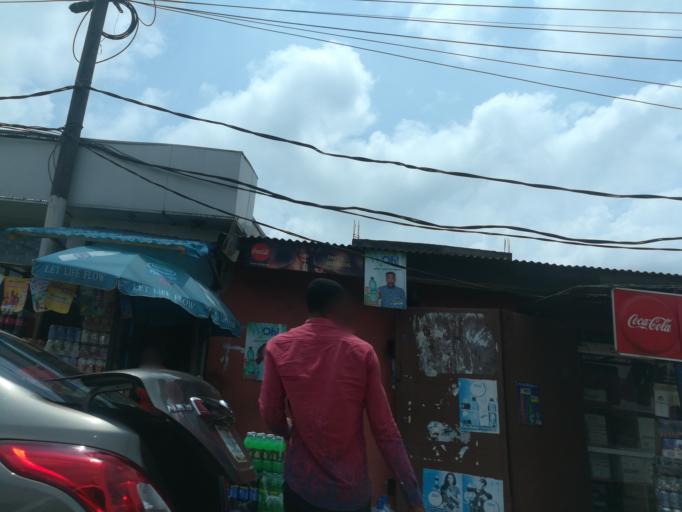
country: NG
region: Lagos
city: Ikeja
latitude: 6.5924
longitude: 3.3605
